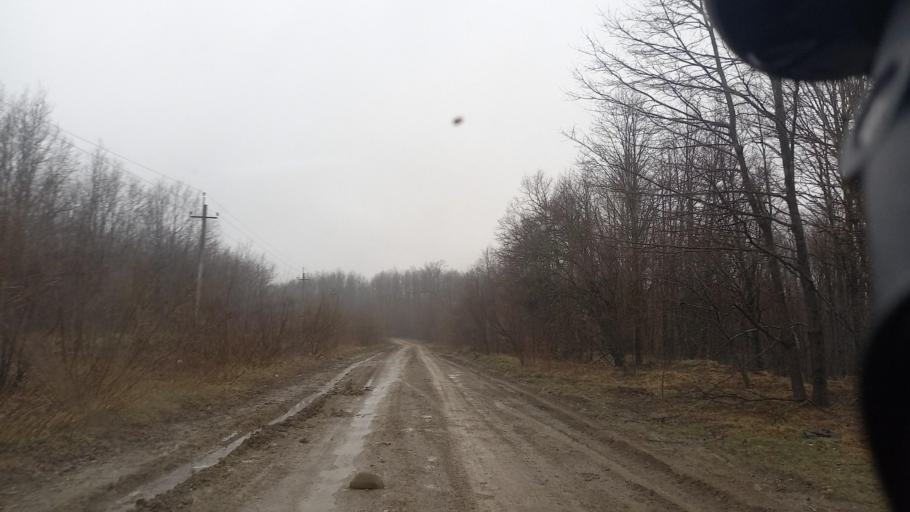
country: RU
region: Krasnodarskiy
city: Saratovskaya
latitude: 44.6322
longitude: 39.2593
